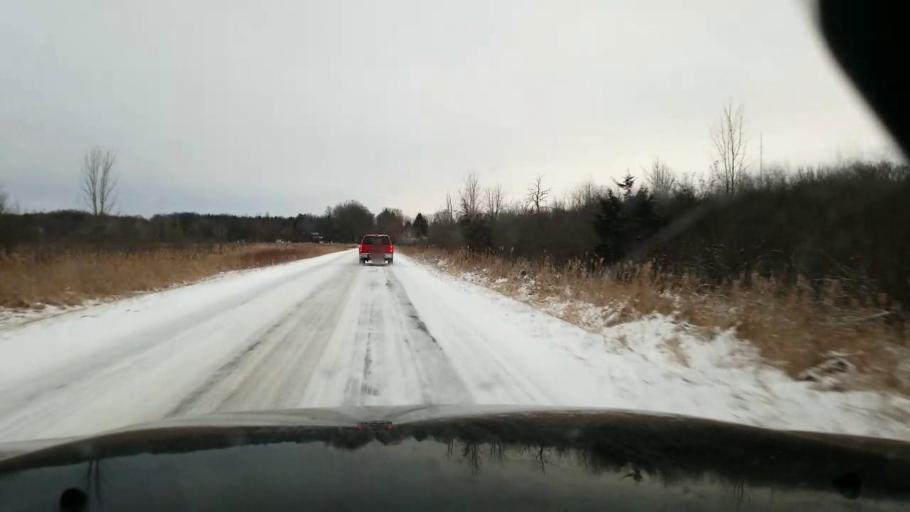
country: US
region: Michigan
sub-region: Jackson County
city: Spring Arbor
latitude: 42.1256
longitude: -84.4983
